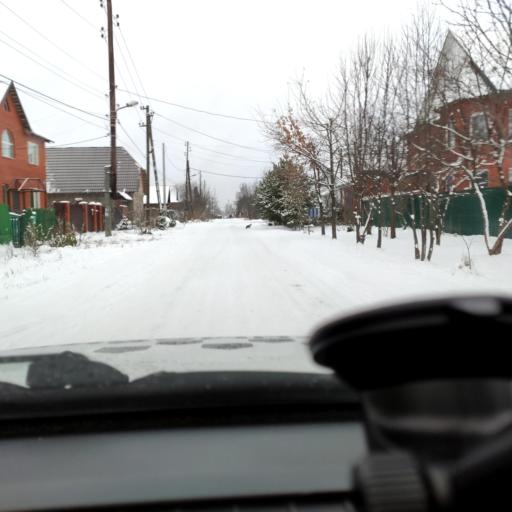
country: RU
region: Perm
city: Perm
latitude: 58.0510
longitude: 56.3563
